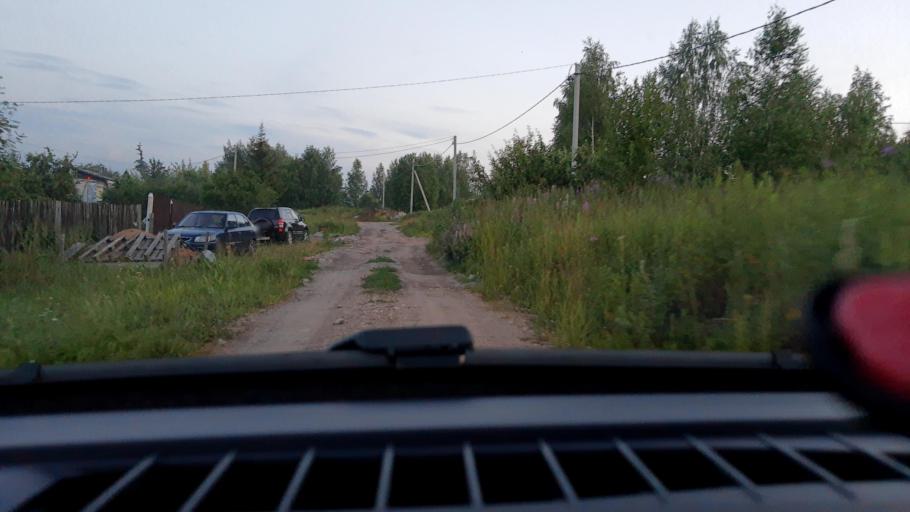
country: RU
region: Nizjnij Novgorod
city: Afonino
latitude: 56.2510
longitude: 44.0656
